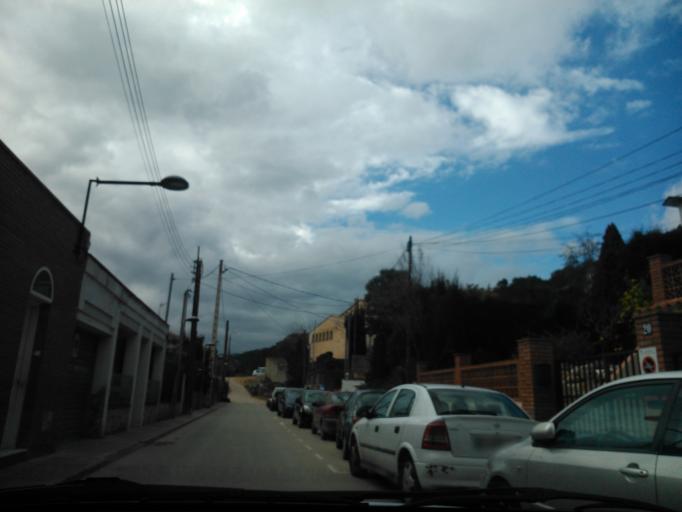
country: ES
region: Catalonia
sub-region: Provincia de Barcelona
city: Cervello
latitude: 41.4133
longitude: 1.9647
